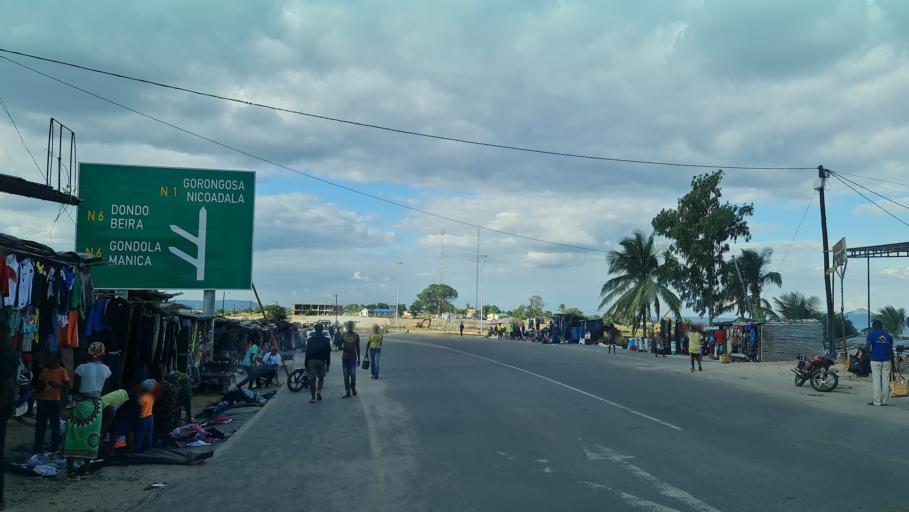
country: MZ
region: Manica
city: Chimoio
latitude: -19.2089
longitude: 33.9305
